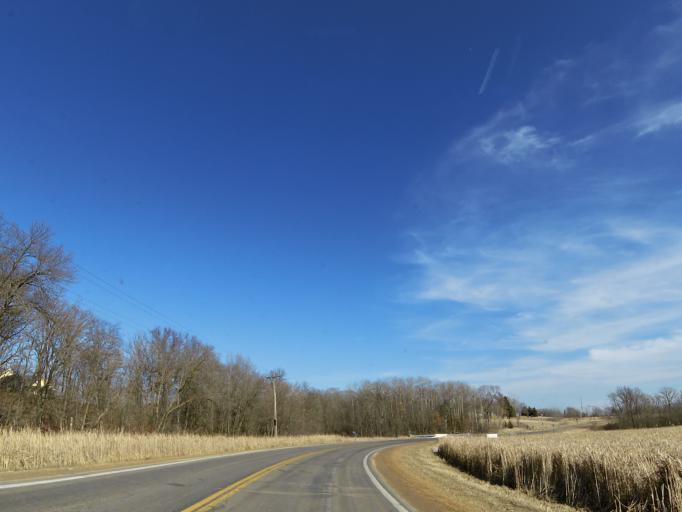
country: US
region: Minnesota
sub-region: Scott County
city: Prior Lake
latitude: 44.6325
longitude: -93.4455
